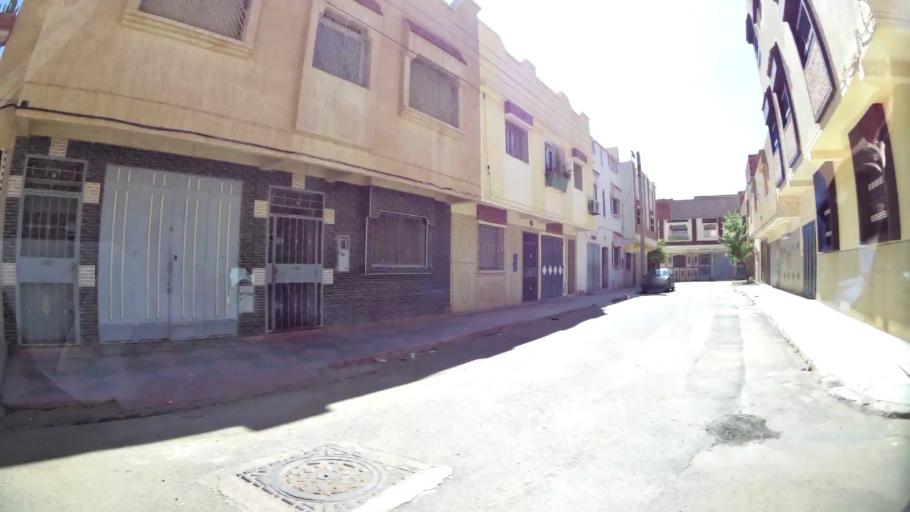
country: MA
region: Oriental
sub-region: Oujda-Angad
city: Oujda
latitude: 34.6610
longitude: -1.9304
